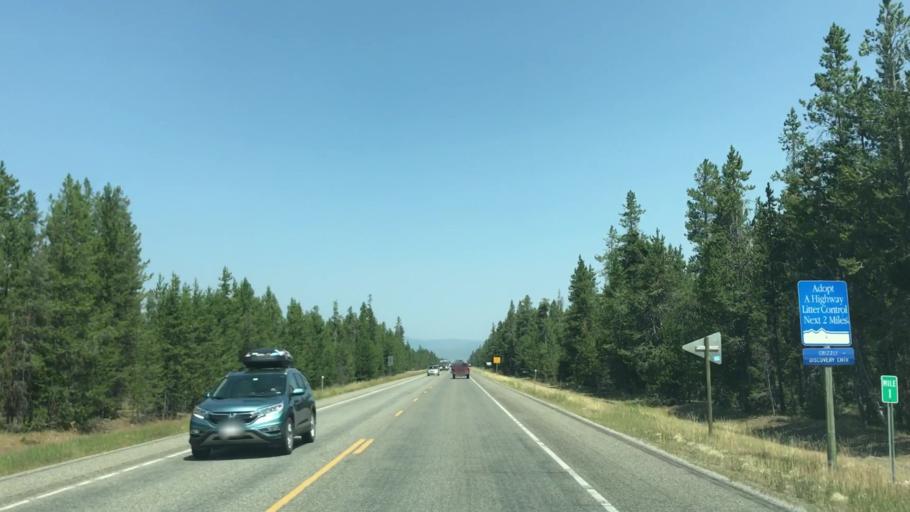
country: US
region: Montana
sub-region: Gallatin County
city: West Yellowstone
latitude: 44.6767
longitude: -111.1005
